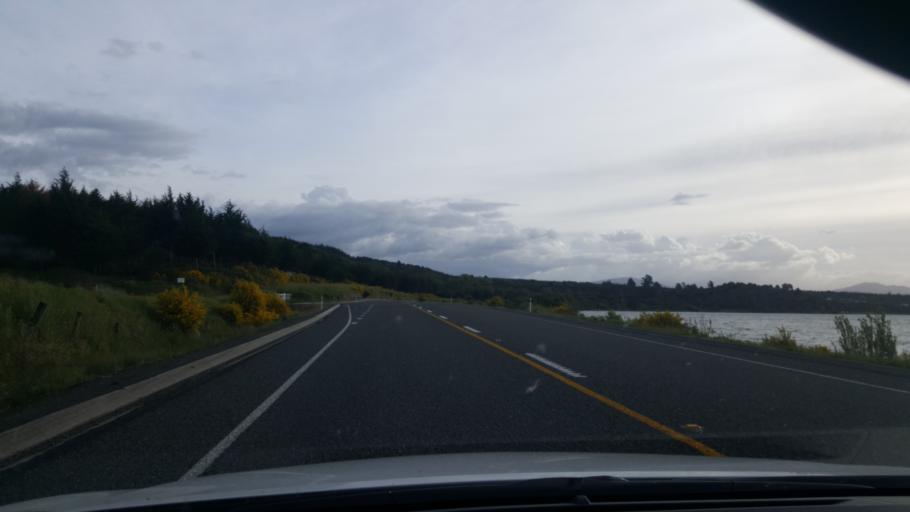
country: NZ
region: Waikato
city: Turangi
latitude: -38.8997
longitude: 175.9448
